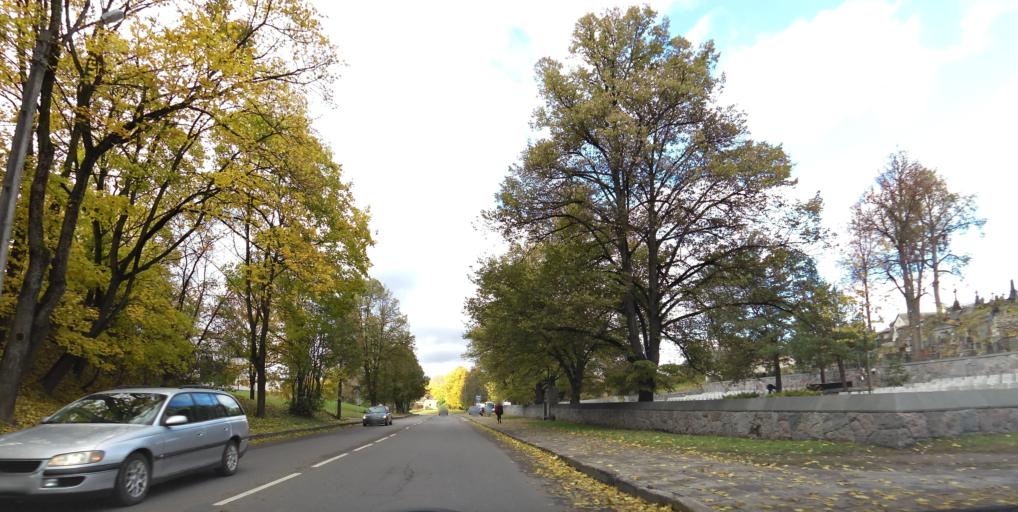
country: LT
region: Vilnius County
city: Rasos
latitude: 54.6699
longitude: 25.3014
